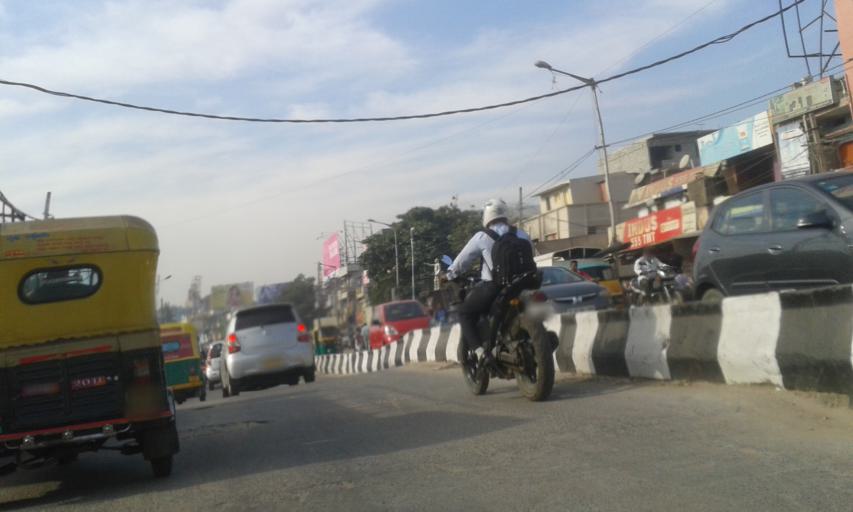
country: IN
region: Karnataka
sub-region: Bangalore Urban
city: Bangalore
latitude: 12.9476
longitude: 77.6194
